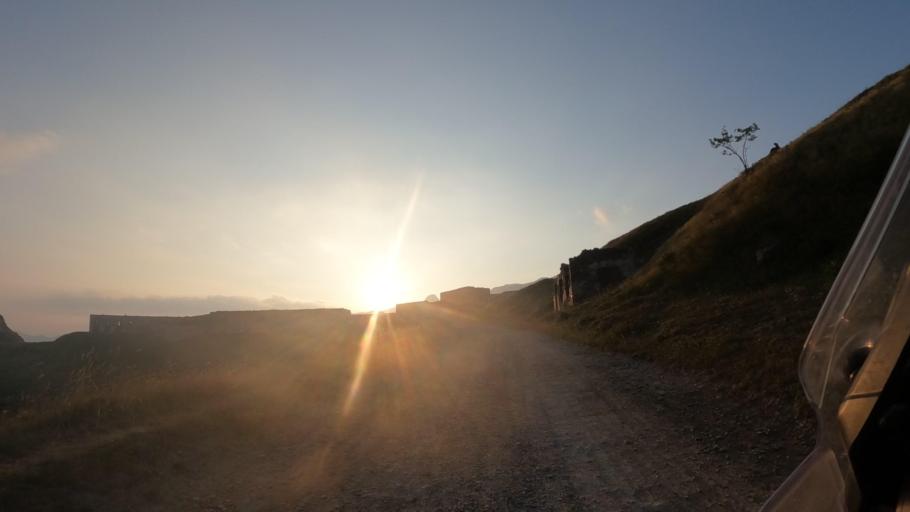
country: IT
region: Piedmont
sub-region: Provincia di Cuneo
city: Limone Piemonte
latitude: 44.1508
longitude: 7.5655
